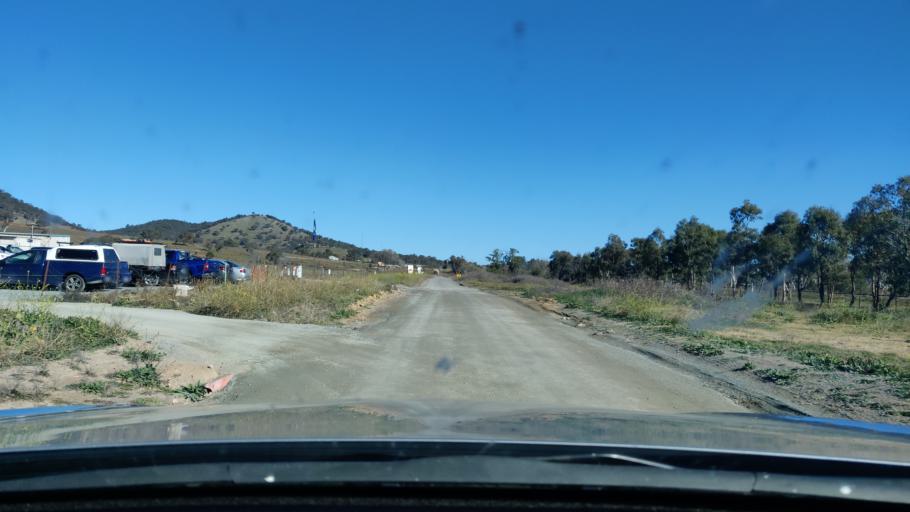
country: AU
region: Australian Capital Territory
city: Macarthur
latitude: -35.4023
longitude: 149.1631
